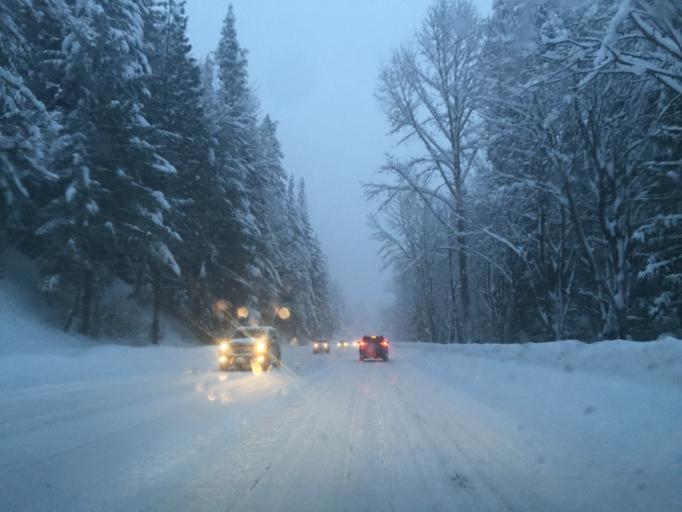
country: US
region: Washington
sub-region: Chelan County
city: Leavenworth
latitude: 47.7912
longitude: -120.8714
